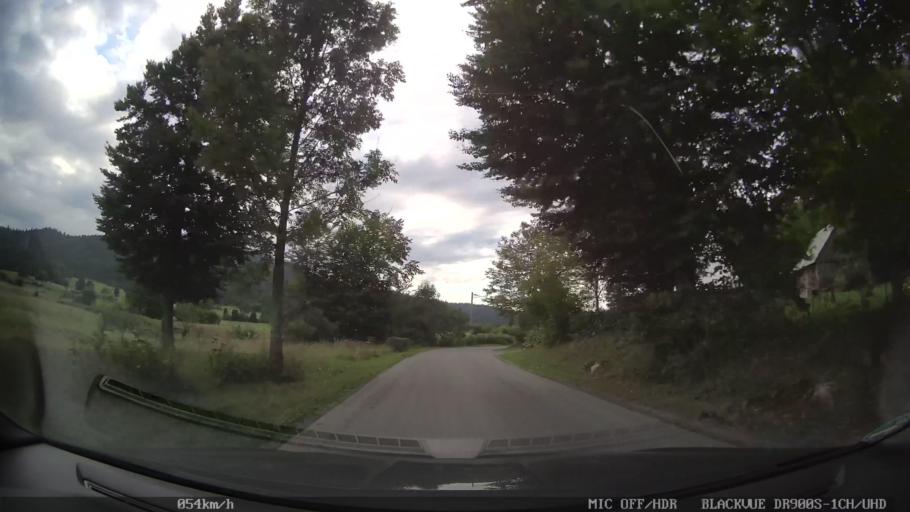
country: HR
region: Licko-Senjska
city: Jezerce
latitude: 44.9445
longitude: 15.5407
